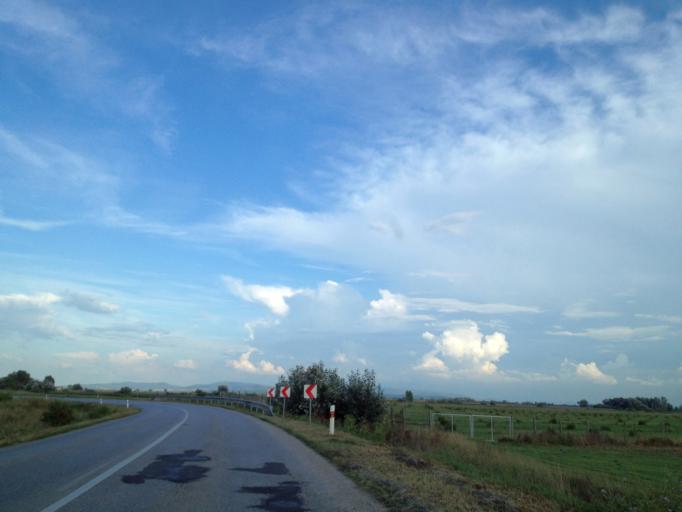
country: SK
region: Nitriansky
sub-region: Okres Komarno
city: Hurbanovo
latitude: 47.8059
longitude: 18.1931
